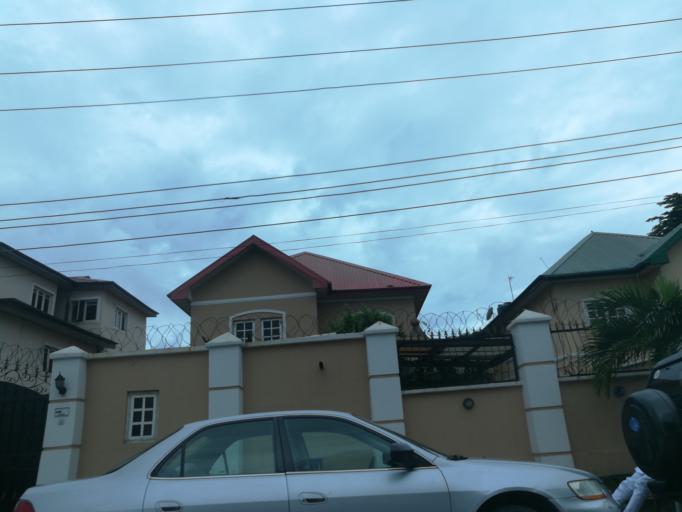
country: NG
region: Lagos
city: Ikoyi
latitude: 6.4487
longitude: 3.4557
